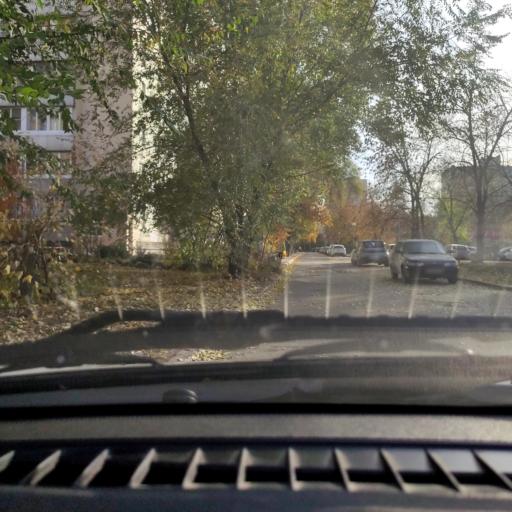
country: RU
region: Samara
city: Tol'yatti
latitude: 53.5355
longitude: 49.2764
